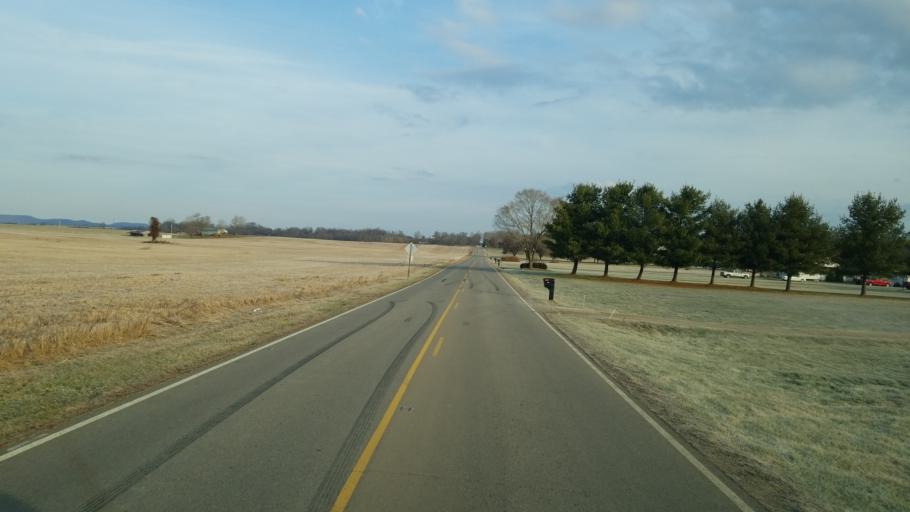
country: US
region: Ohio
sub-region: Ross County
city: Chillicothe
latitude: 39.2532
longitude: -82.8709
